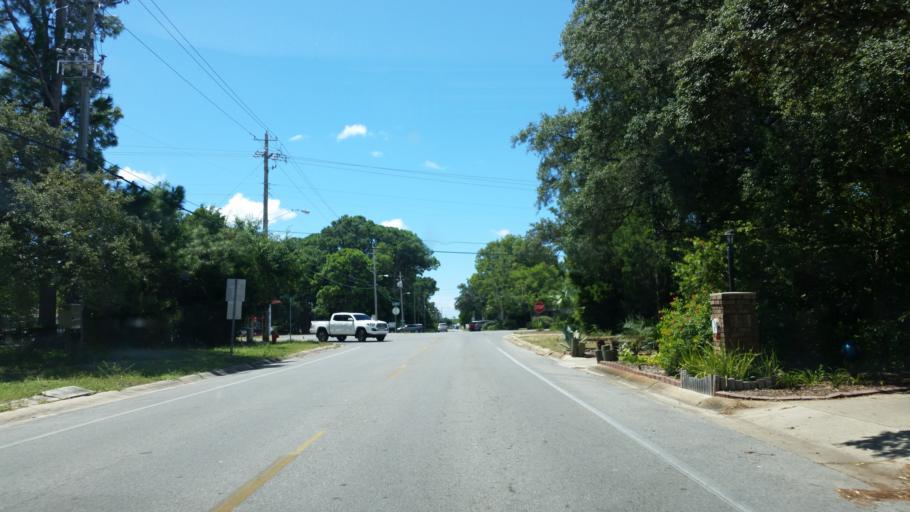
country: US
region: Florida
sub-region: Okaloosa County
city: Fort Walton Beach
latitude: 30.4128
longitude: -86.5996
